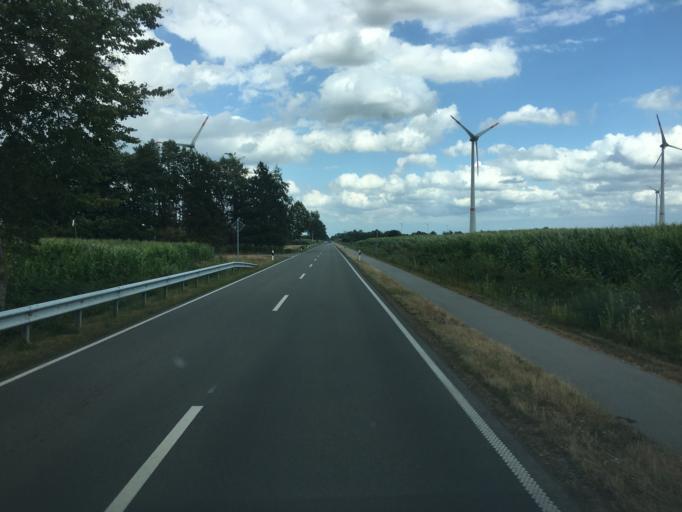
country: DE
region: Lower Saxony
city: Barssel
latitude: 53.0751
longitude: 7.7343
